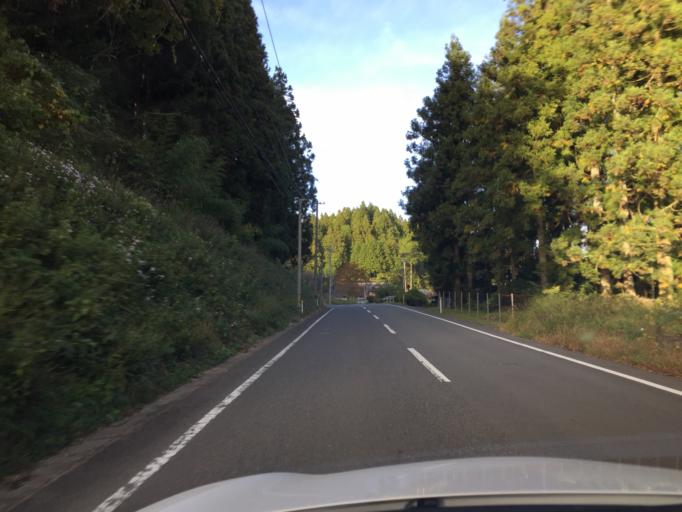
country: JP
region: Fukushima
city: Ishikawa
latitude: 37.1933
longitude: 140.5830
